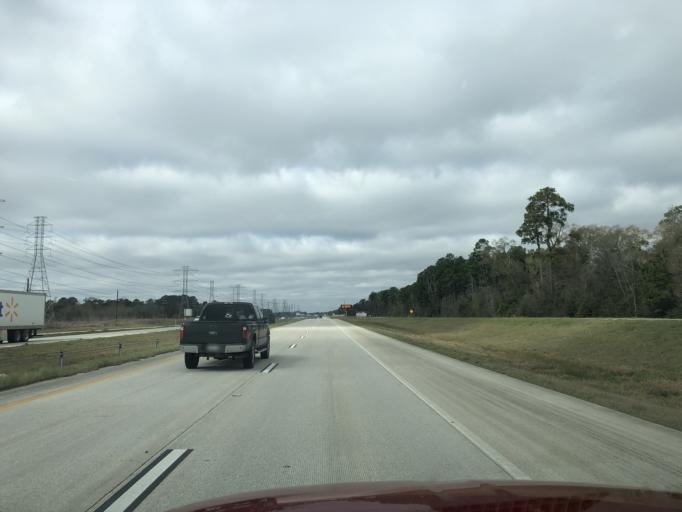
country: US
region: Texas
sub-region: Harris County
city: Spring
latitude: 30.0898
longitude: -95.4605
